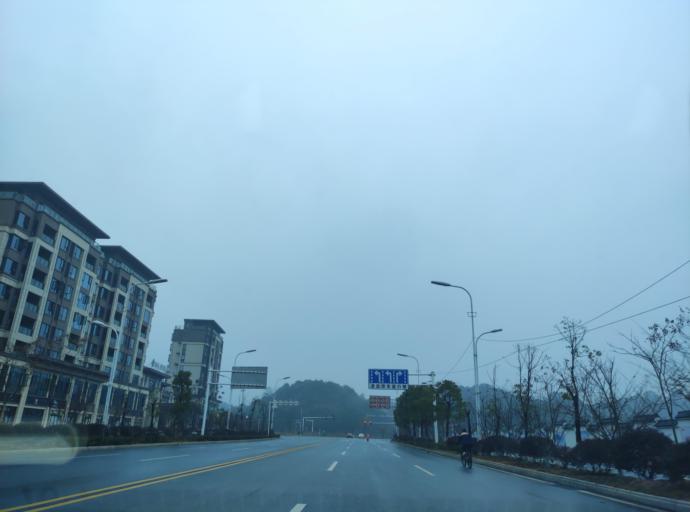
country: CN
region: Jiangxi Sheng
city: Pingxiang
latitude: 27.6681
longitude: 113.8479
